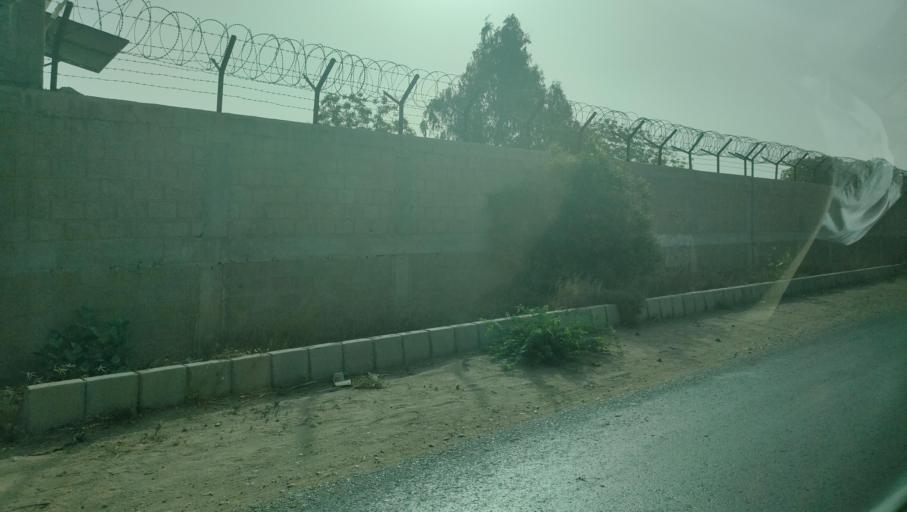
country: PK
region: Sindh
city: Malir Cantonment
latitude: 24.9158
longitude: 67.1883
